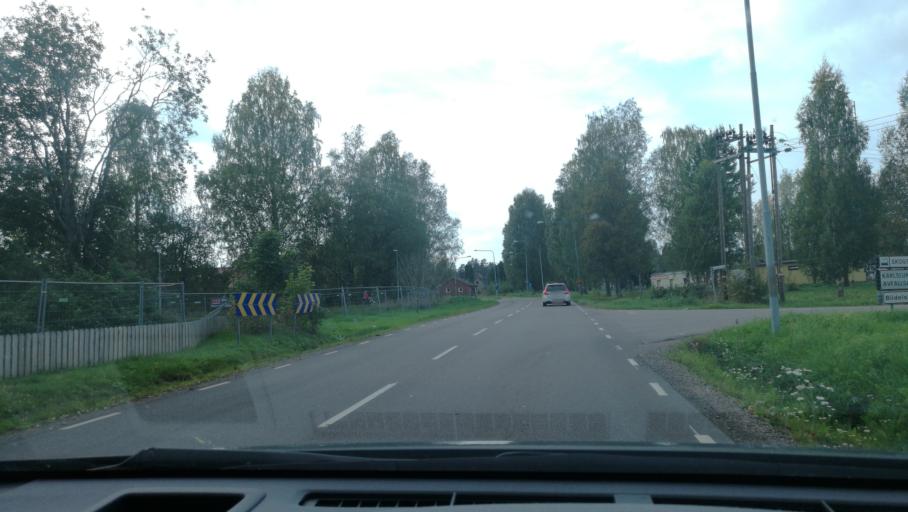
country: SE
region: Dalarna
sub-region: Avesta Kommun
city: Avesta
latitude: 60.1624
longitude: 16.1919
